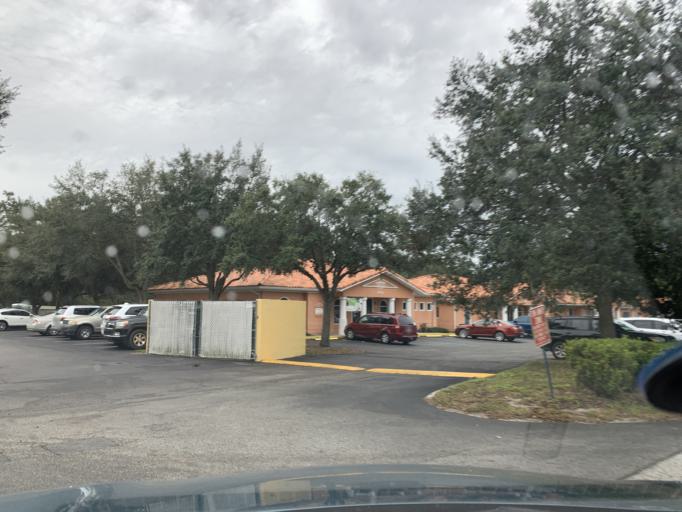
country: US
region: Florida
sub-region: Pasco County
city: Zephyrhills North
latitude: 28.2591
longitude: -82.1891
